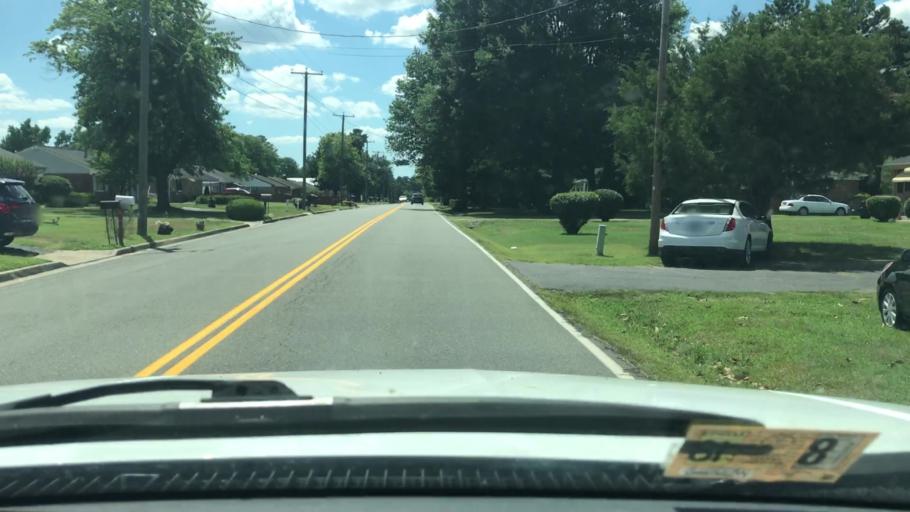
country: US
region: Virginia
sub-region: Henrico County
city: East Highland Park
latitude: 37.5705
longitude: -77.3945
